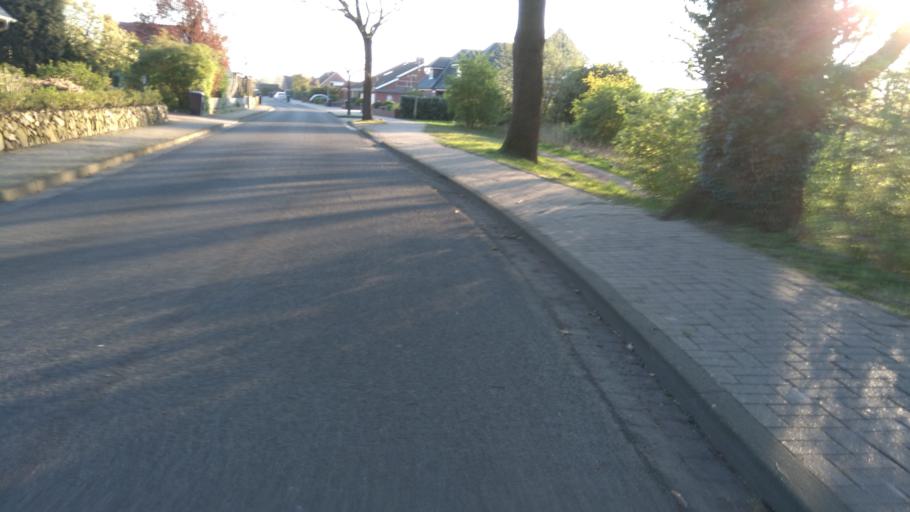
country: DE
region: Lower Saxony
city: Harsefeld
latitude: 53.4625
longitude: 9.5048
